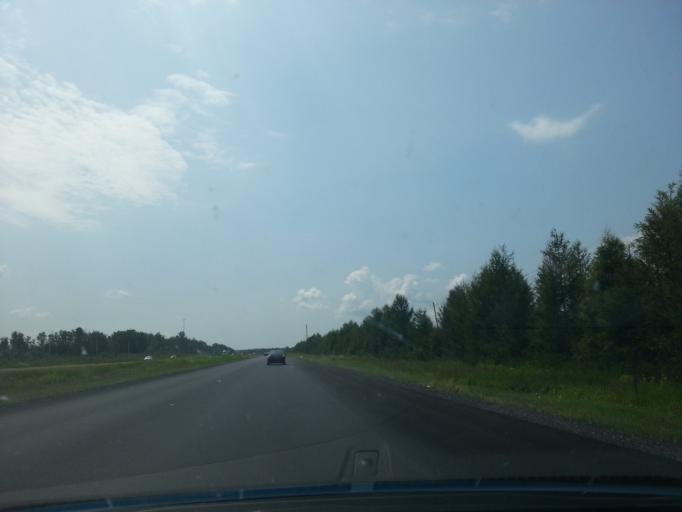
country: CA
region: Quebec
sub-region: Mauricie
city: Plessisville
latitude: 46.4154
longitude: -71.8089
